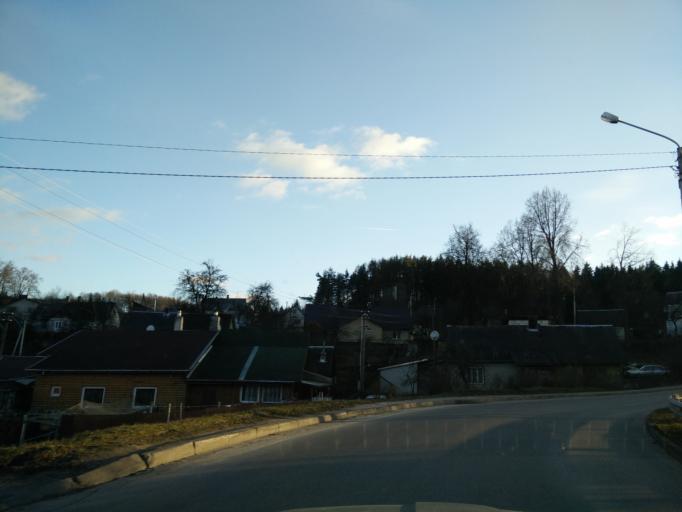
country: LT
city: Skaidiskes
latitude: 54.6916
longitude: 25.3975
